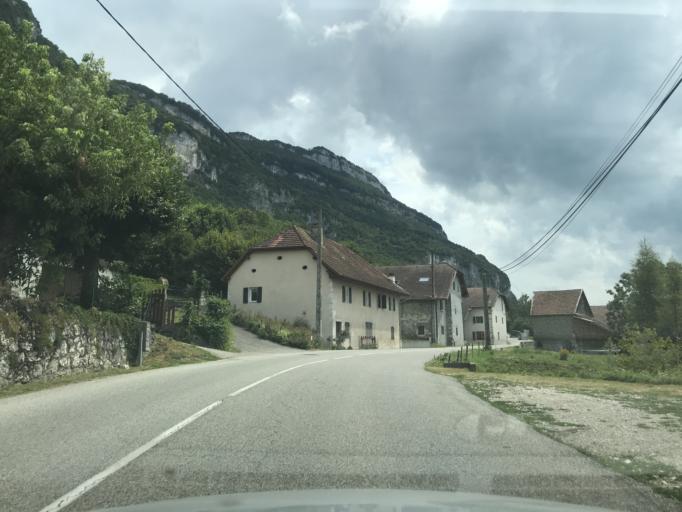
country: FR
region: Rhone-Alpes
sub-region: Departement de la Savoie
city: Chatillon
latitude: 45.8025
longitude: 5.8566
